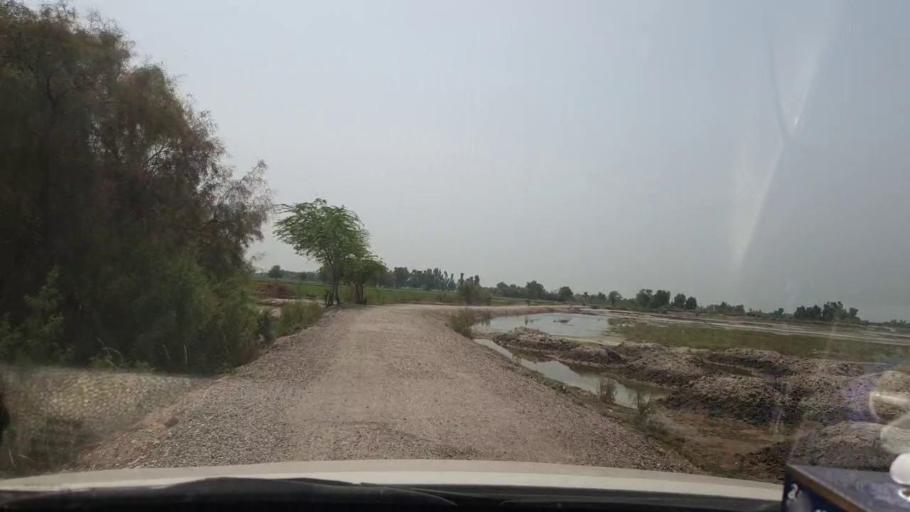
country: PK
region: Sindh
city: Shikarpur
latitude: 27.9872
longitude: 68.7061
